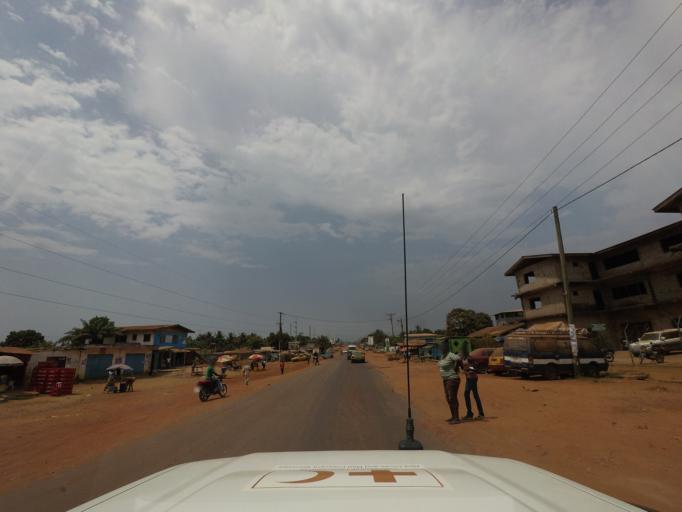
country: LR
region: Montserrado
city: Monrovia
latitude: 6.2804
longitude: -10.6920
